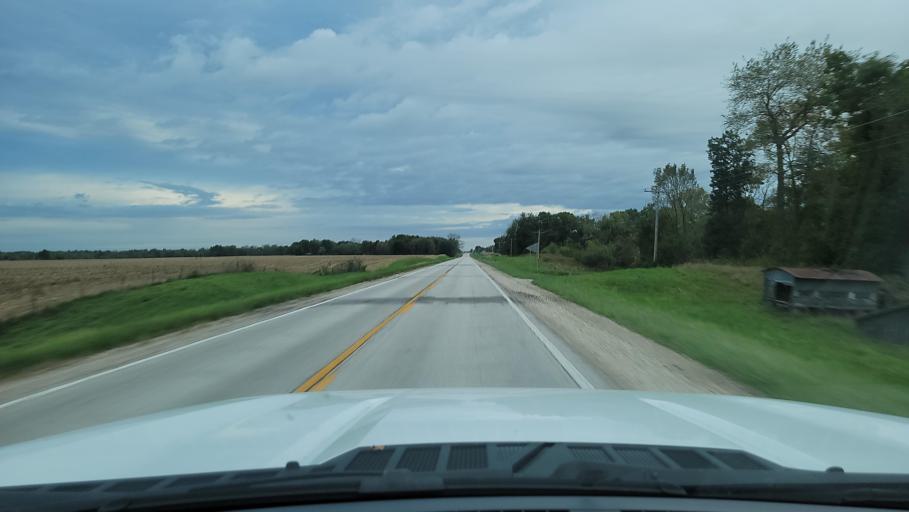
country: US
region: Illinois
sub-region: Schuyler County
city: Rushville
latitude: 40.0506
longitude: -90.6152
